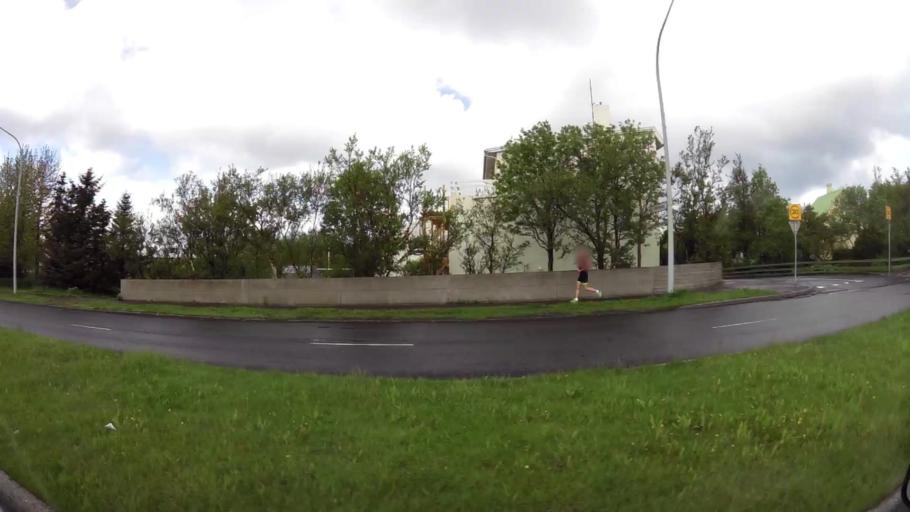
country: IS
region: Capital Region
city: Seltjarnarnes
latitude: 64.1366
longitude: -21.9552
